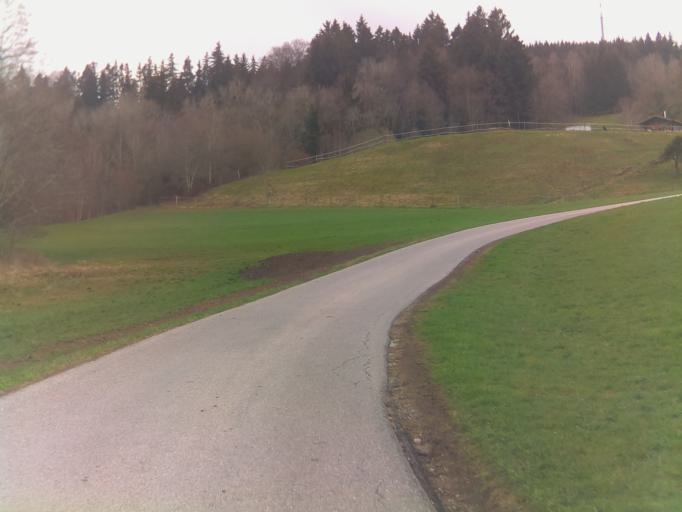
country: DE
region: Bavaria
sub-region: Upper Bavaria
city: Hohenpeissenberg
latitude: 47.8109
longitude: 11.0331
